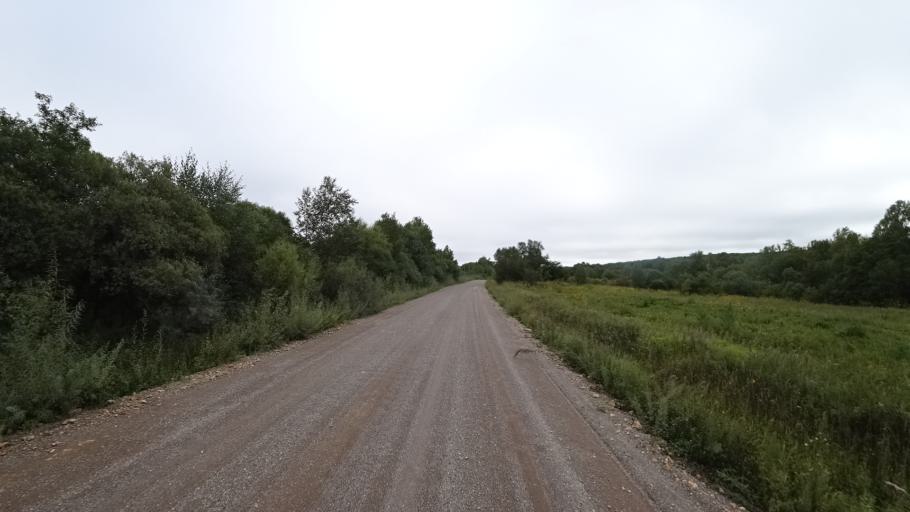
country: RU
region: Primorskiy
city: Ivanovka
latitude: 44.0473
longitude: 132.4912
